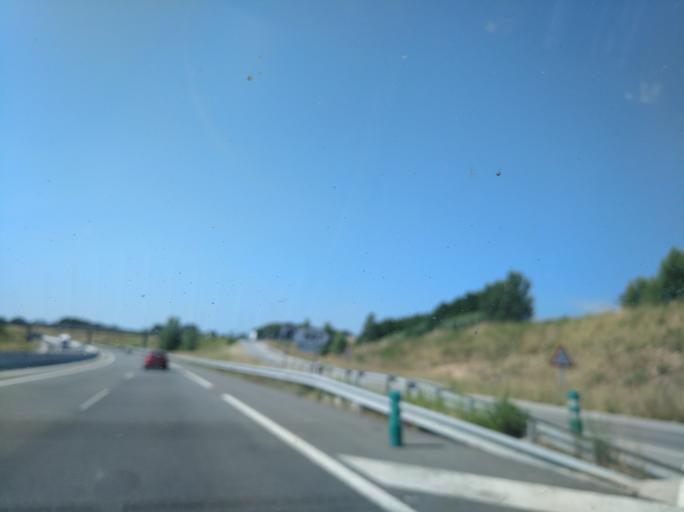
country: ES
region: Catalonia
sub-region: Provincia de Girona
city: Sils
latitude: 41.8365
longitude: 2.7589
